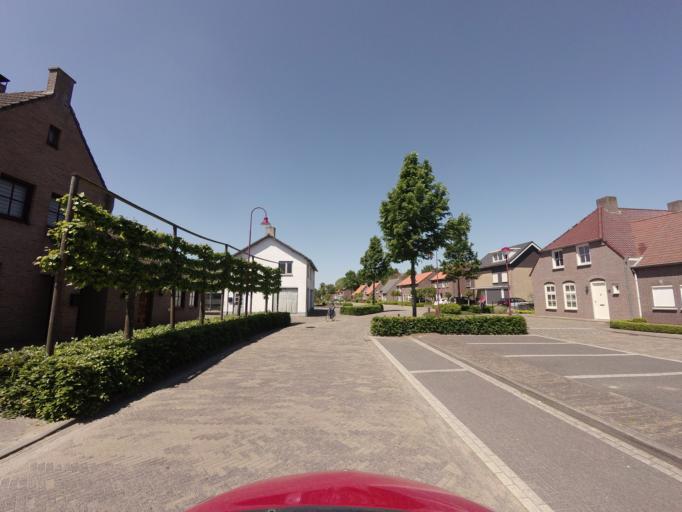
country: NL
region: North Brabant
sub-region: Bergeijk
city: Bergeyk
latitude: 51.2900
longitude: 5.3194
